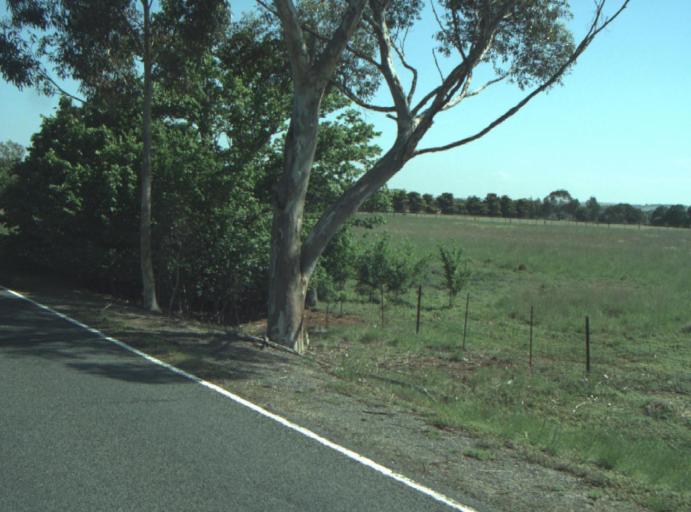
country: AU
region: Victoria
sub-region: Greater Geelong
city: Lara
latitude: -38.0040
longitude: 144.3998
